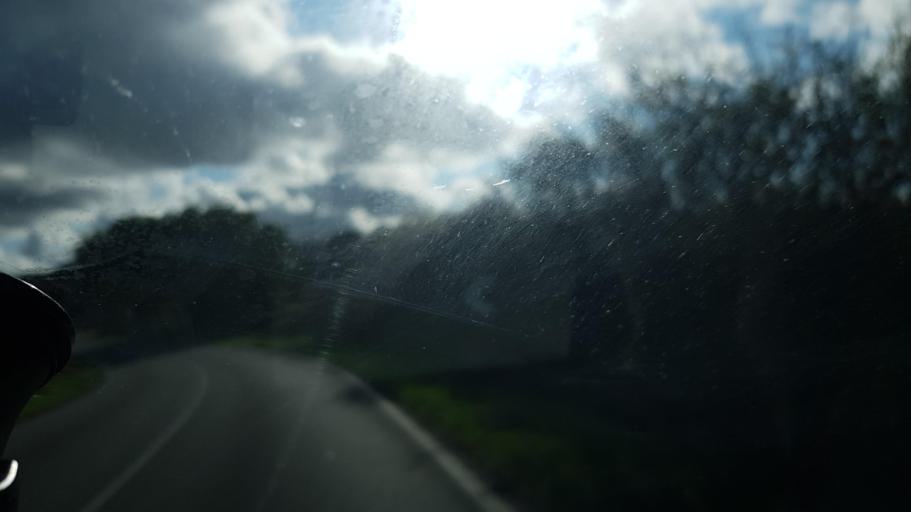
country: IT
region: Apulia
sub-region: Provincia di Brindisi
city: Ostuni
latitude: 40.6871
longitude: 17.5886
